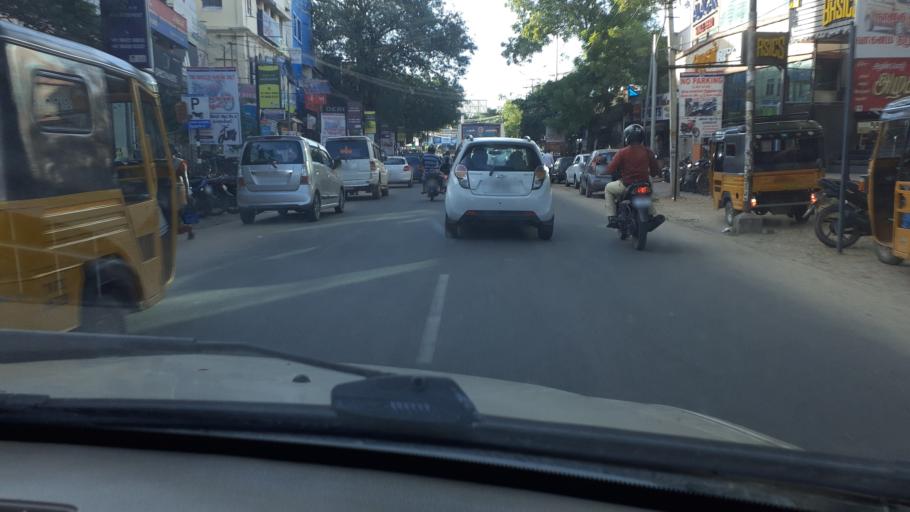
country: IN
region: Tamil Nadu
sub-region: Tirunelveli Kattabo
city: Tirunelveli
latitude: 8.7258
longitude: 77.7307
